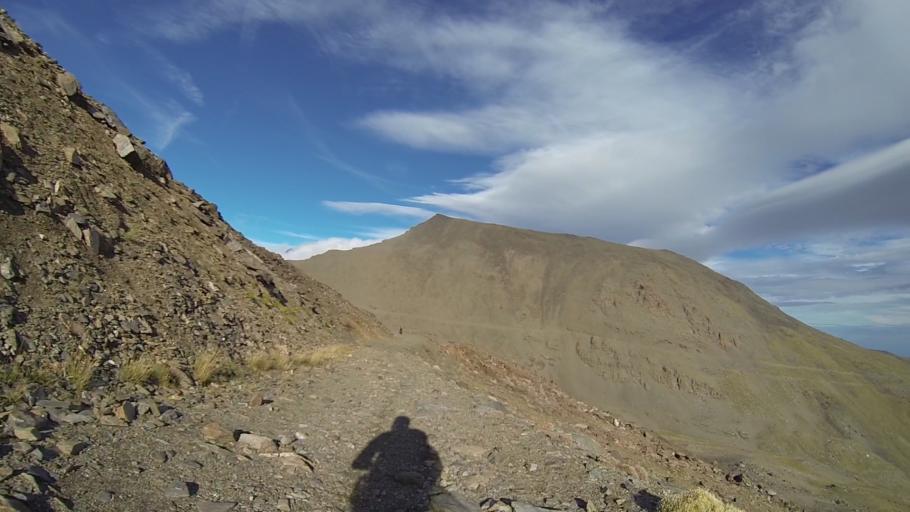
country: ES
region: Andalusia
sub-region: Provincia de Granada
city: Trevelez
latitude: 37.0476
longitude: -3.3316
